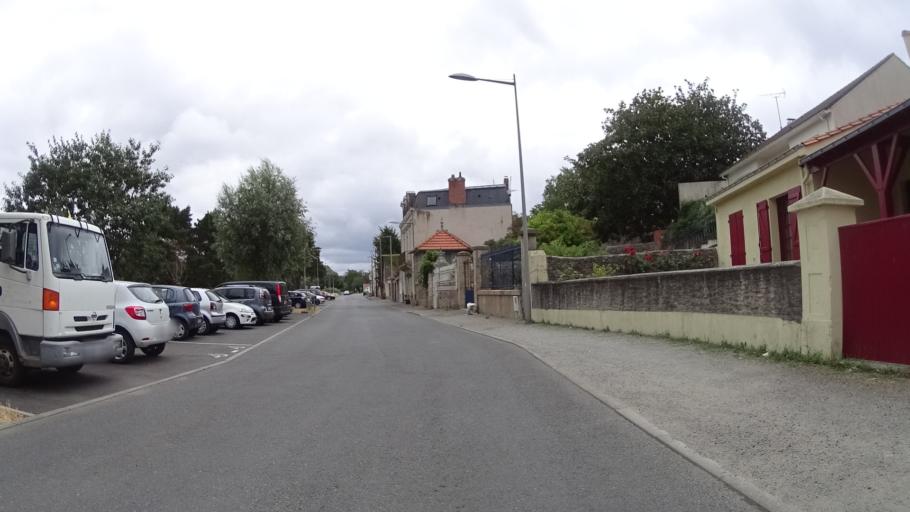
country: FR
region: Pays de la Loire
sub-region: Departement de la Loire-Atlantique
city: Le Pellerin
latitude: 47.2019
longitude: -1.7516
